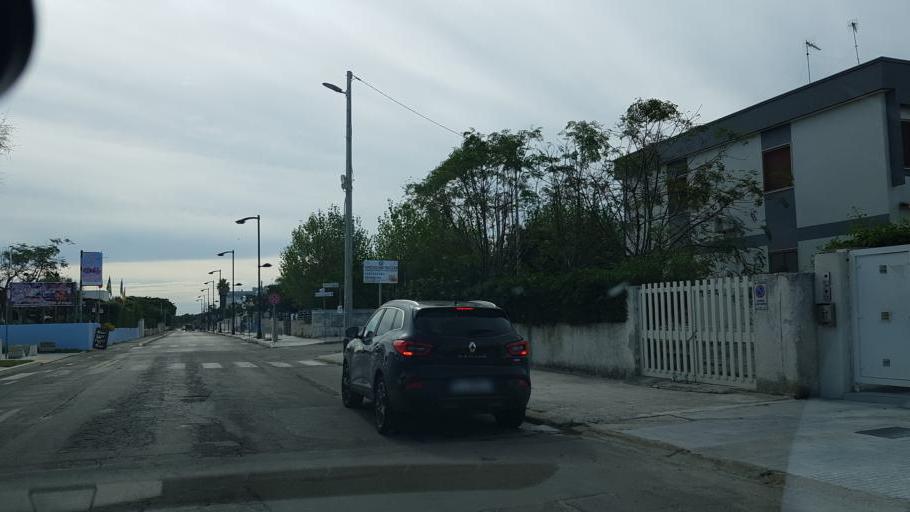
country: IT
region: Apulia
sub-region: Provincia di Lecce
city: Borgagne
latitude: 40.3007
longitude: 18.4061
